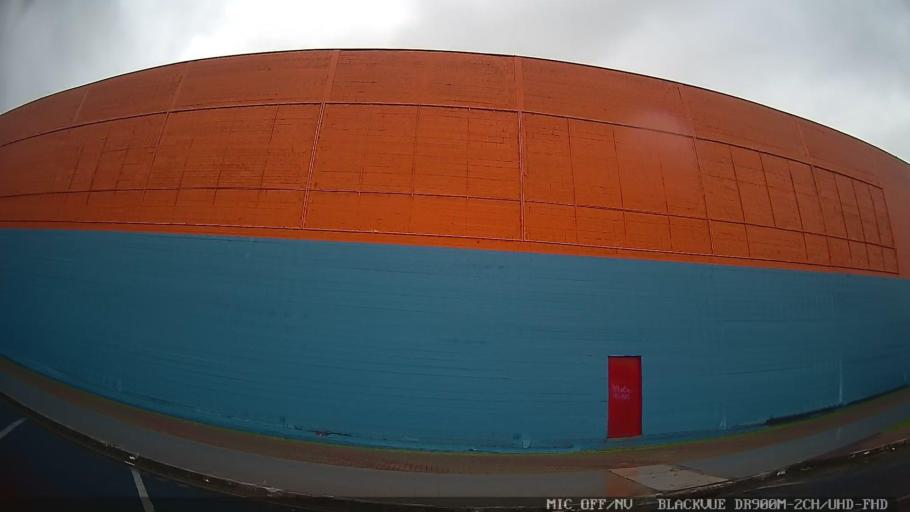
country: BR
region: Sao Paulo
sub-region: Itanhaem
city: Itanhaem
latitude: -24.1763
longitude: -46.7781
